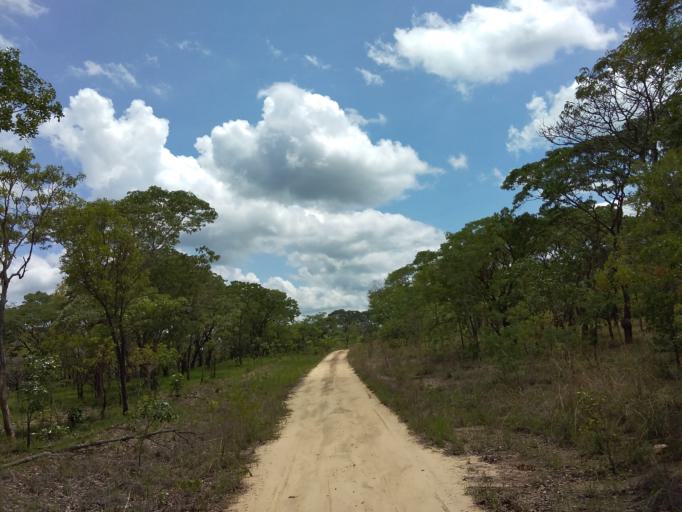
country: ZM
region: Central
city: Mkushi
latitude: -14.0651
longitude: 29.9601
